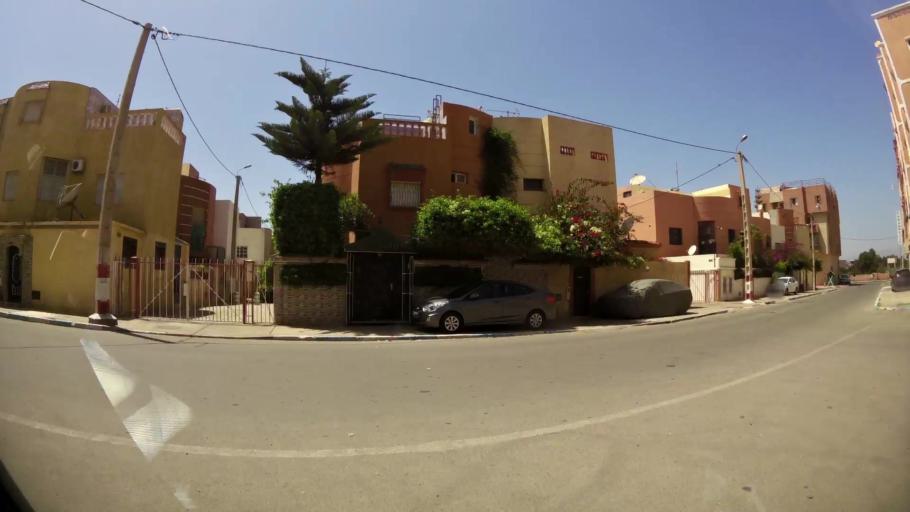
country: MA
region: Souss-Massa-Draa
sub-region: Inezgane-Ait Mellou
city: Inezgane
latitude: 30.3518
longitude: -9.4895
